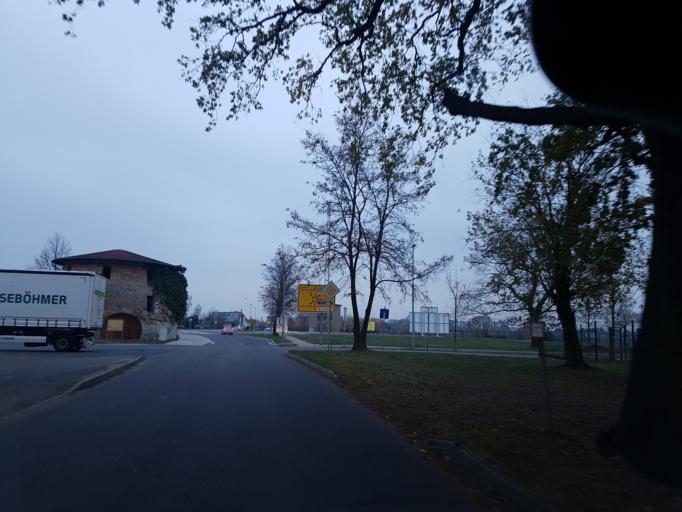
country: DE
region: Brandenburg
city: Finsterwalde
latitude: 51.6364
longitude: 13.7291
